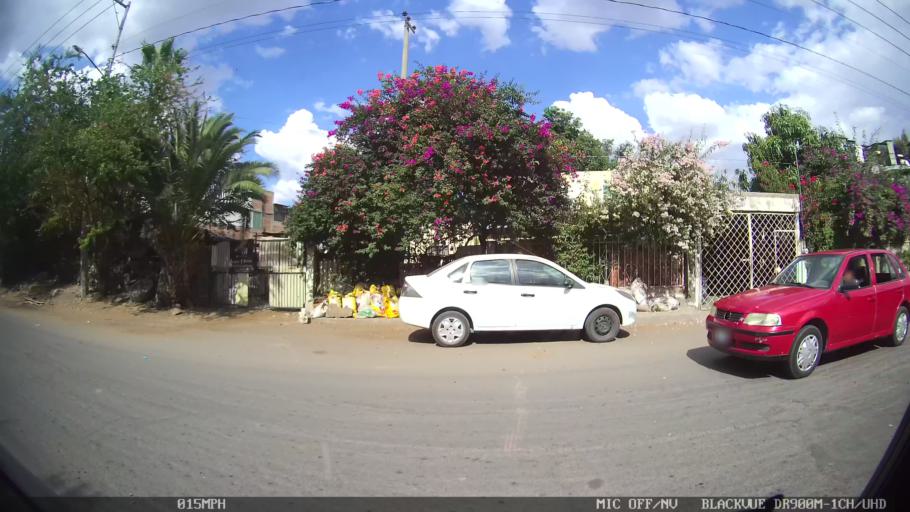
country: MX
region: Jalisco
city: Tlaquepaque
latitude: 20.6623
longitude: -103.2677
